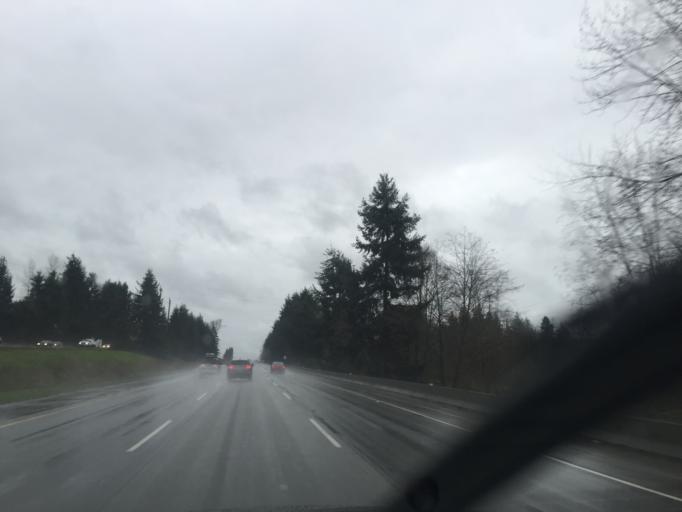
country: CA
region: British Columbia
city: Langley
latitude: 49.1309
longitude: -122.5680
